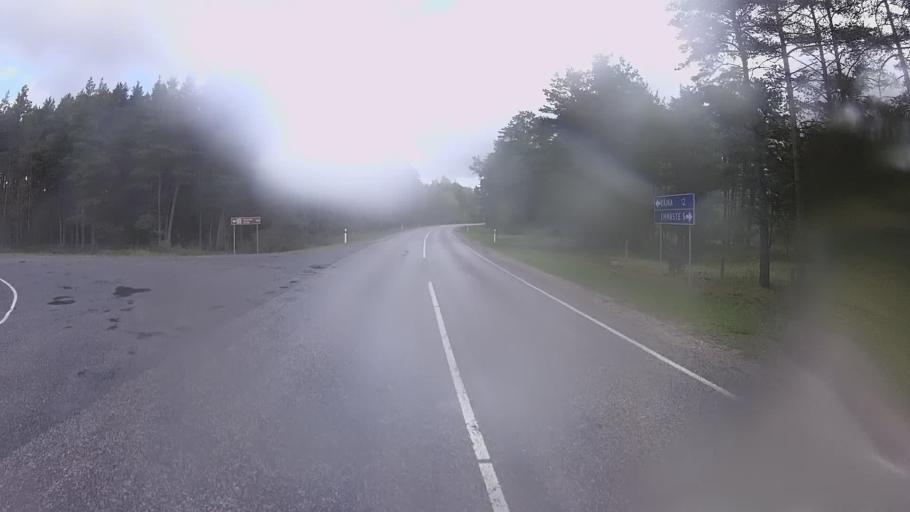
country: EE
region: Hiiumaa
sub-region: Kaerdla linn
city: Kardla
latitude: 58.7565
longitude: 22.6363
